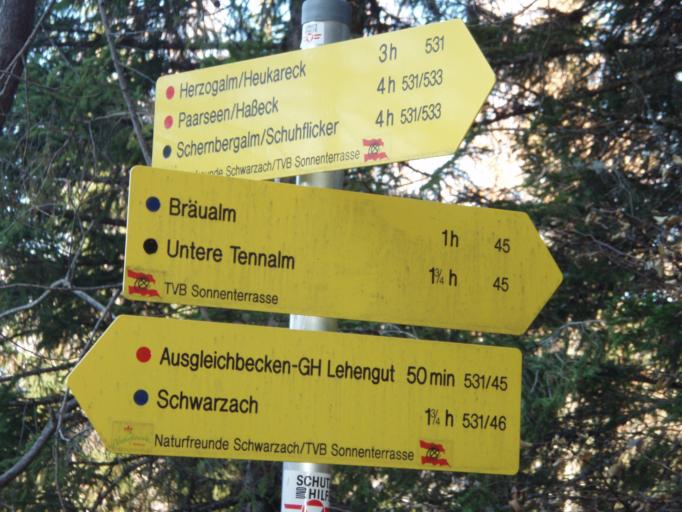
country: AT
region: Salzburg
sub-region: Politischer Bezirk Sankt Johann im Pongau
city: Schwarzach im Pongau
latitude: 47.3053
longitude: 13.1453
